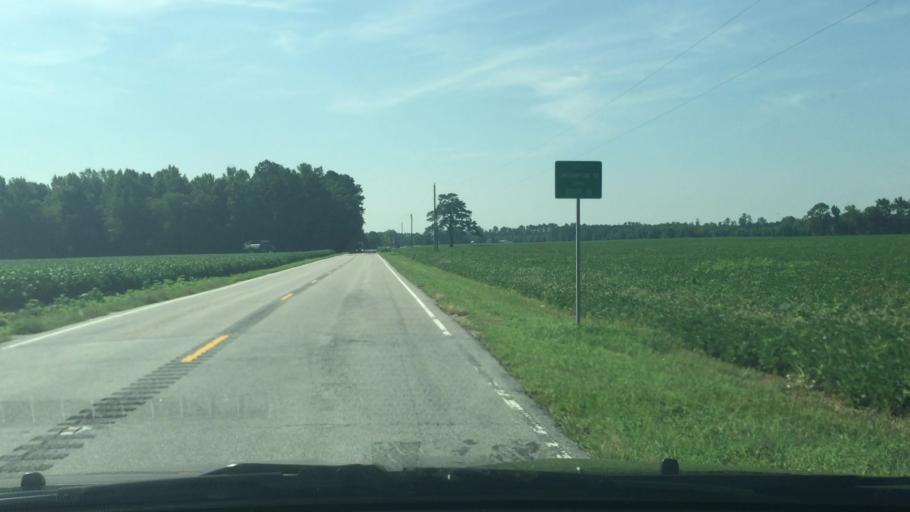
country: US
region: Virginia
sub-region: Southampton County
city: Courtland
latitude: 36.8517
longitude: -77.1341
